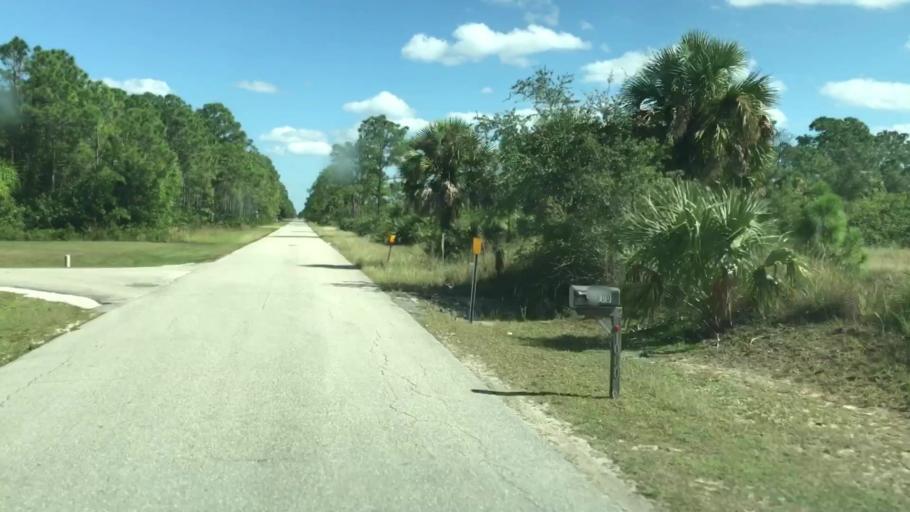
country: US
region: Florida
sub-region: Lee County
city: Lehigh Acres
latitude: 26.6282
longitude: -81.6453
